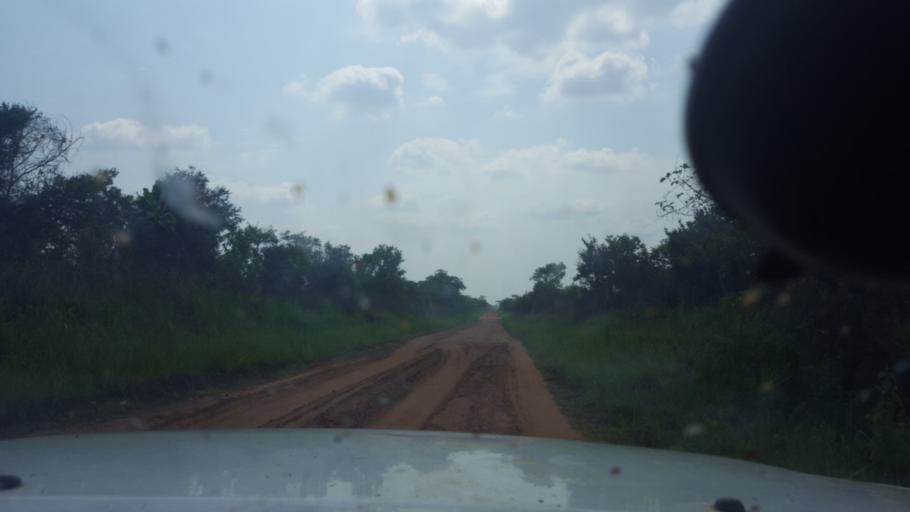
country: CD
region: Bandundu
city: Bandundu
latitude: -3.7620
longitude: 17.1468
